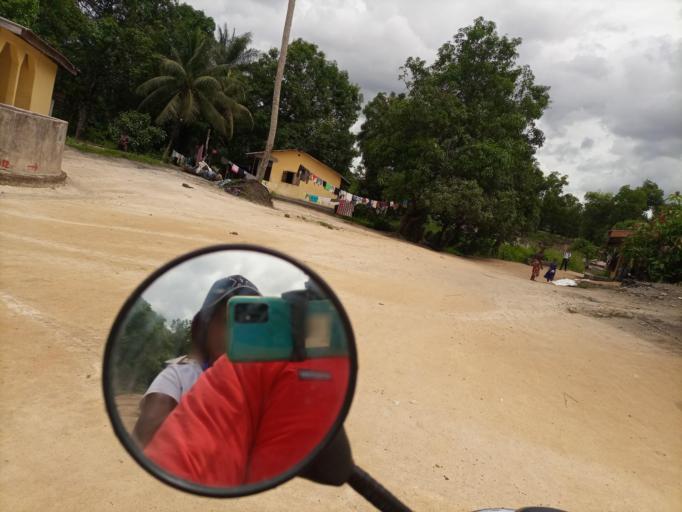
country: SL
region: Southern Province
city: Bo
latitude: 7.9733
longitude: -11.7242
